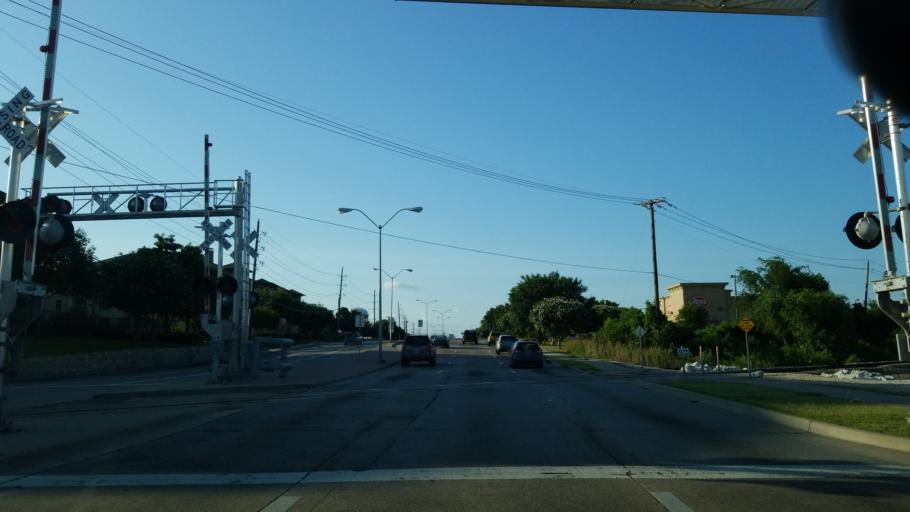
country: US
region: Texas
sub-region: Dallas County
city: Carrollton
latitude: 32.9698
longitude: -96.8899
